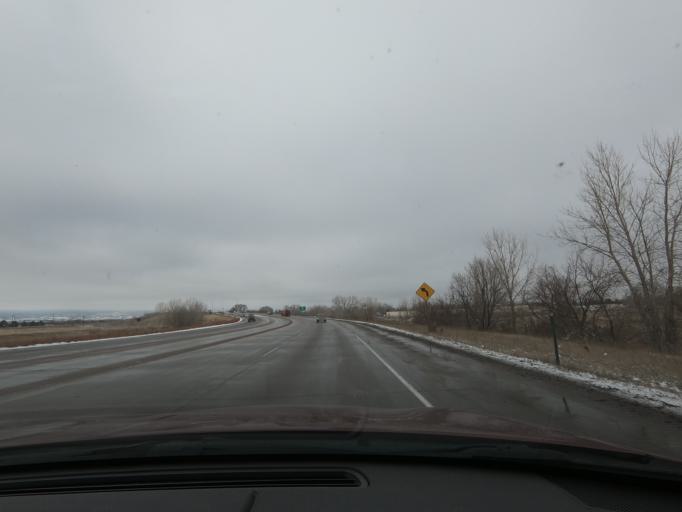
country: US
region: Colorado
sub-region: El Paso County
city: Security-Widefield
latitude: 38.7217
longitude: -104.7124
